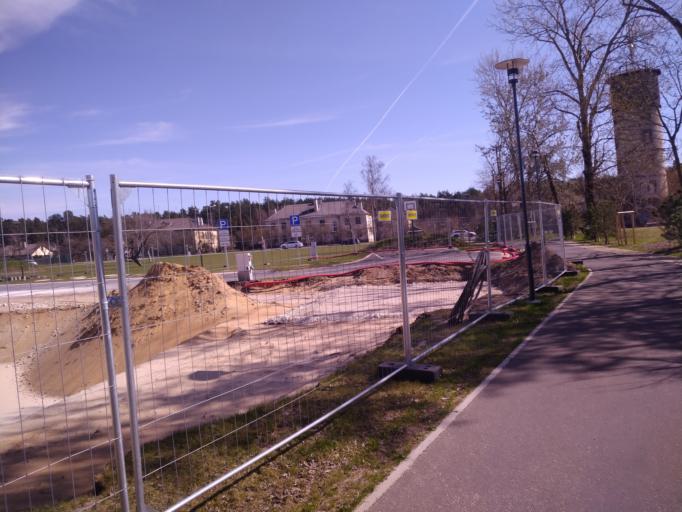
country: LV
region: Stopini
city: Ulbroka
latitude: 56.9380
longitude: 24.2239
